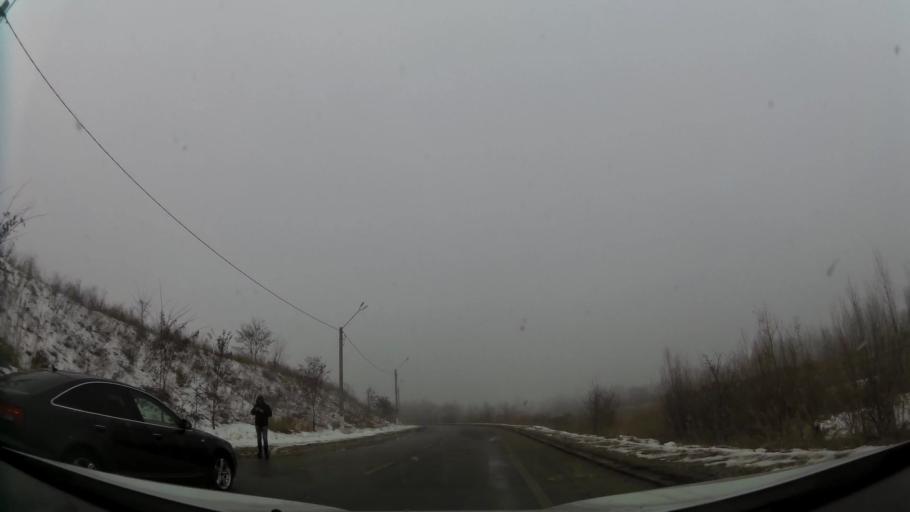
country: RO
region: Ilfov
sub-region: Comuna Chiajna
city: Chiajna
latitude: 44.4661
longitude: 25.9837
